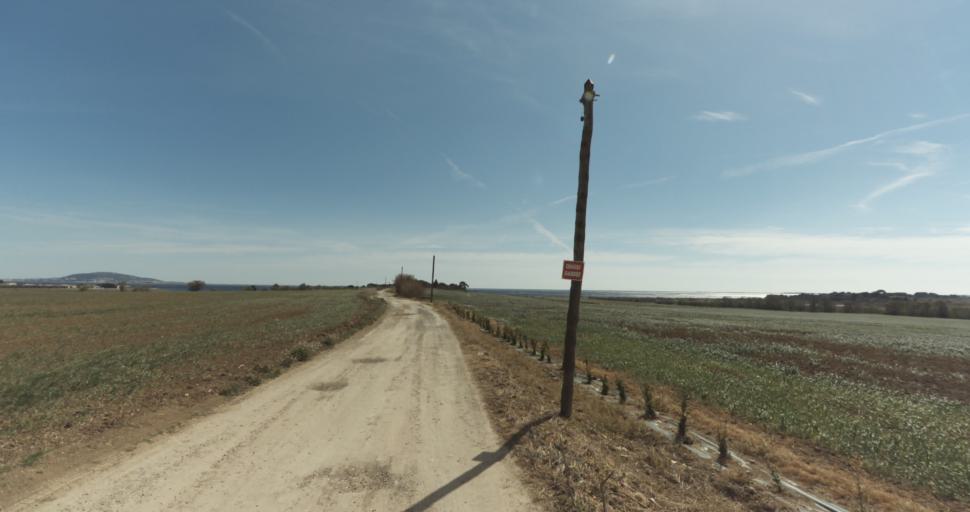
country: FR
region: Languedoc-Roussillon
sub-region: Departement de l'Herault
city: Pinet
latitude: 43.4030
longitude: 3.5555
